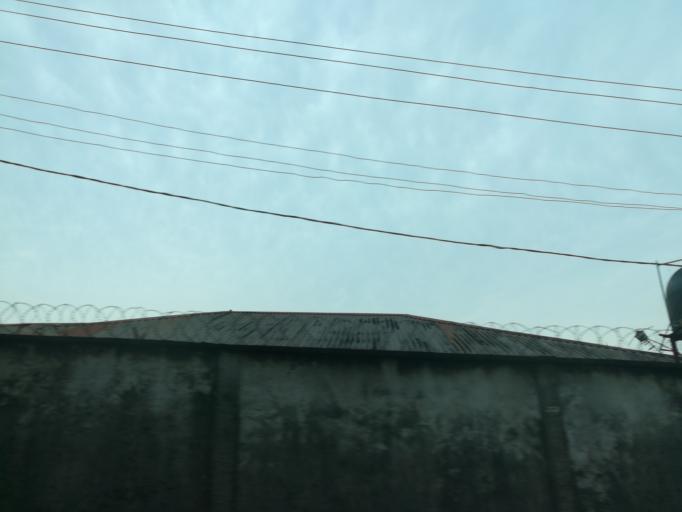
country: NG
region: Rivers
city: Port Harcourt
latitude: 4.8267
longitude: 7.0206
